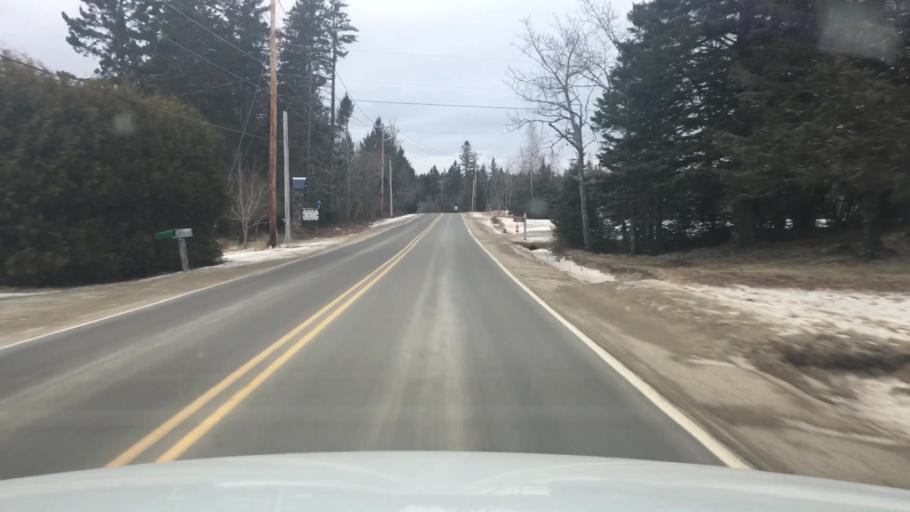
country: US
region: Maine
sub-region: Washington County
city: Addison
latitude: 44.6230
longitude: -67.7118
